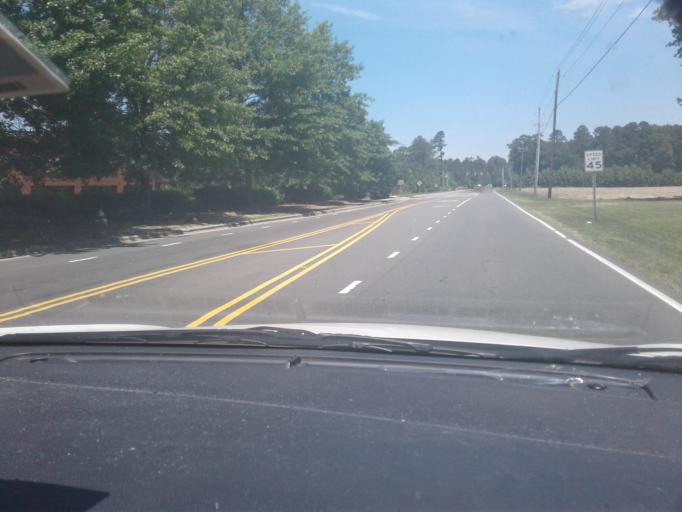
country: US
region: North Carolina
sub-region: Wake County
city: Fuquay-Varina
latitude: 35.5954
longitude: -78.7743
